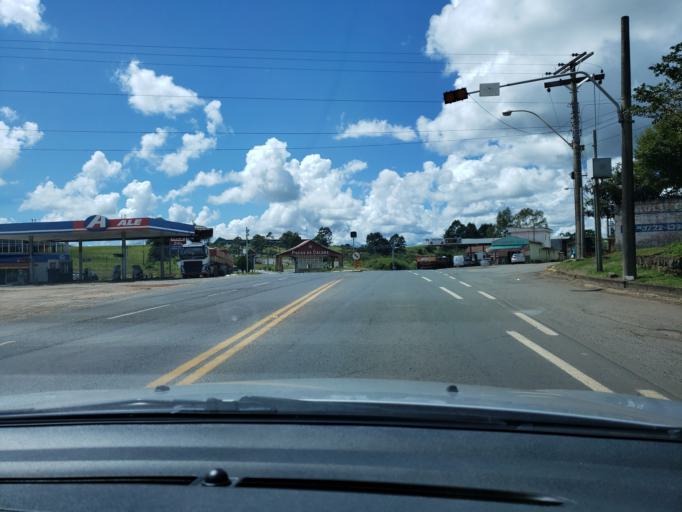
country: BR
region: Minas Gerais
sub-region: Pocos De Caldas
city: Pocos de Caldas
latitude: -21.8456
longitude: -46.6809
